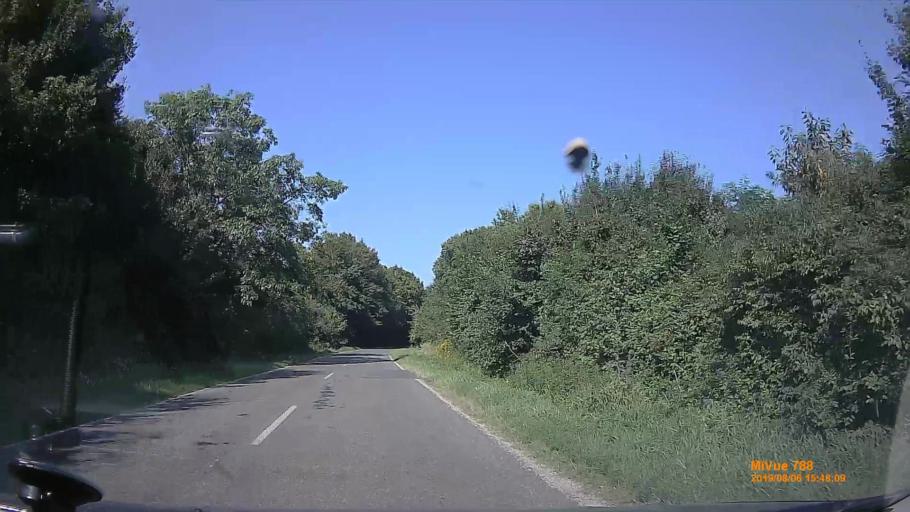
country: HU
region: Somogy
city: Csurgo
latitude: 46.2655
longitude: 17.0314
